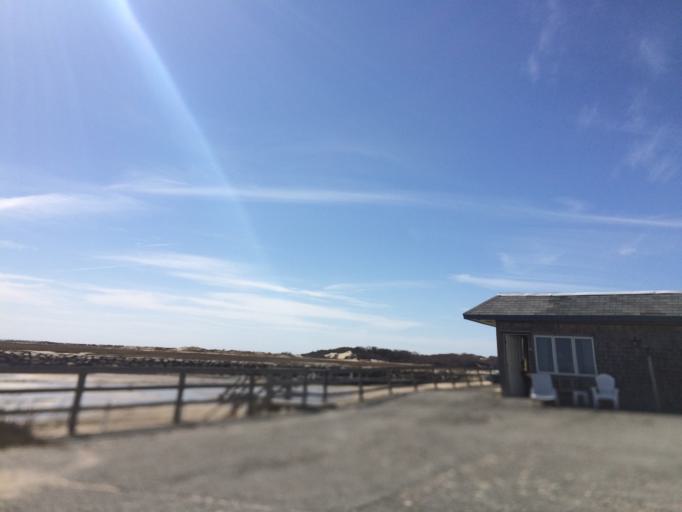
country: US
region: Massachusetts
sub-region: Barnstable County
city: Provincetown
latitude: 42.0363
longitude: -70.1947
